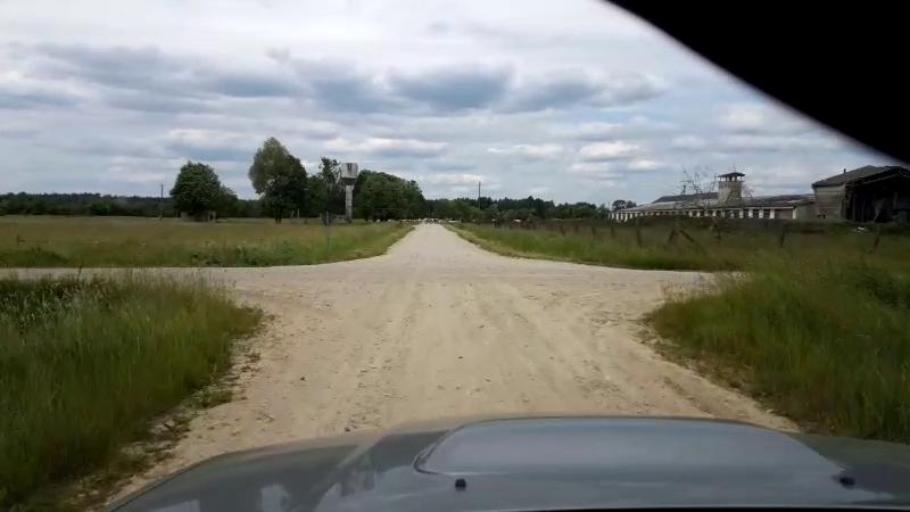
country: EE
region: Paernumaa
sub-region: Sauga vald
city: Sauga
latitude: 58.5100
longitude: 24.5807
